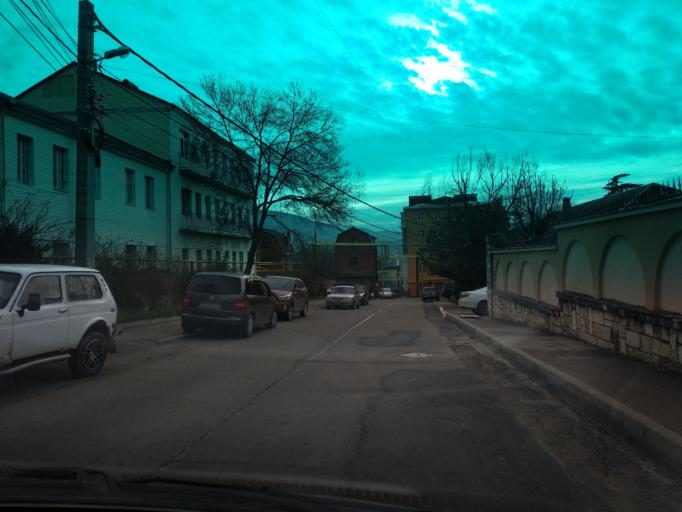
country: RU
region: Krasnodarskiy
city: Tuapse
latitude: 44.1063
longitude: 39.0827
